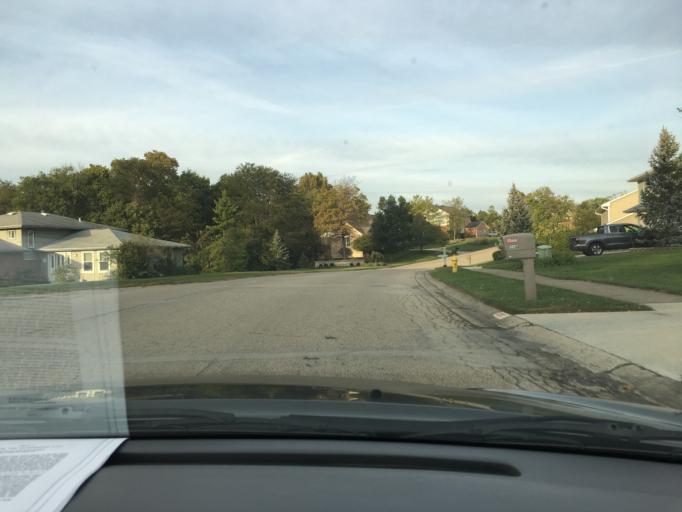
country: US
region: Ohio
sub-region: Butler County
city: Beckett Ridge
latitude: 39.3575
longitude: -84.4472
